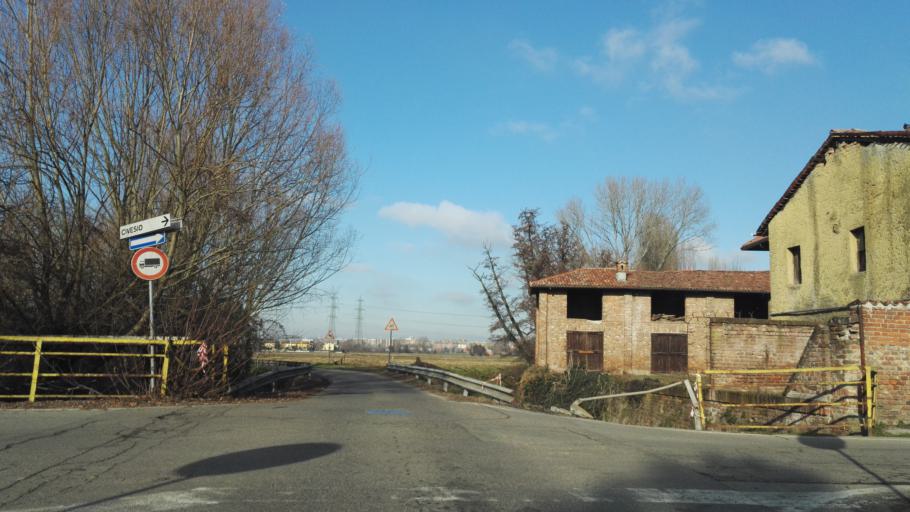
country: IT
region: Lombardy
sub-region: Citta metropolitana di Milano
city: Civesio
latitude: 45.3854
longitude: 9.2741
